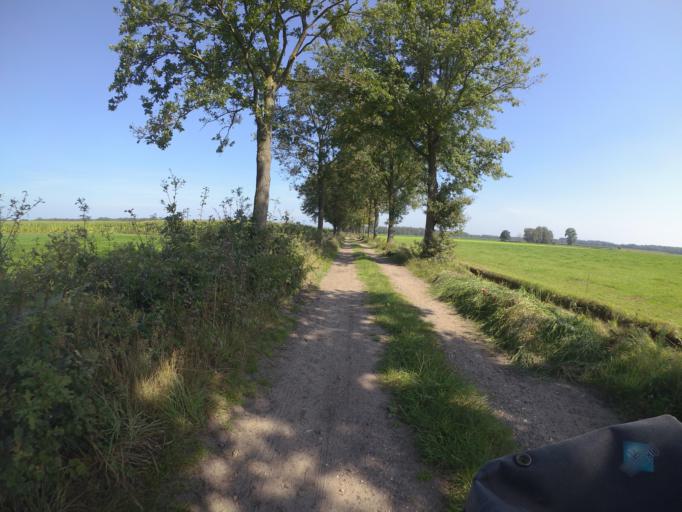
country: NL
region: North Brabant
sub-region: Gemeente Mill en Sint Hubert
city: Wilbertoord
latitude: 51.5578
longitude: 5.7866
